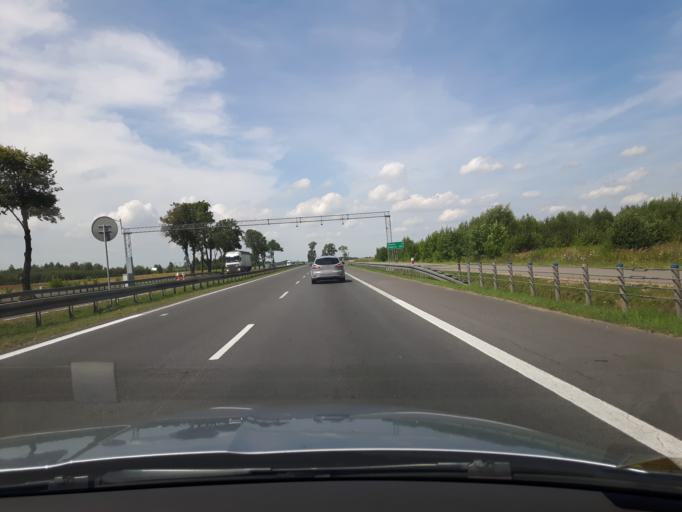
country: PL
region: Masovian Voivodeship
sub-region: Powiat plonski
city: Plonsk
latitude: 52.5897
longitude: 20.4491
